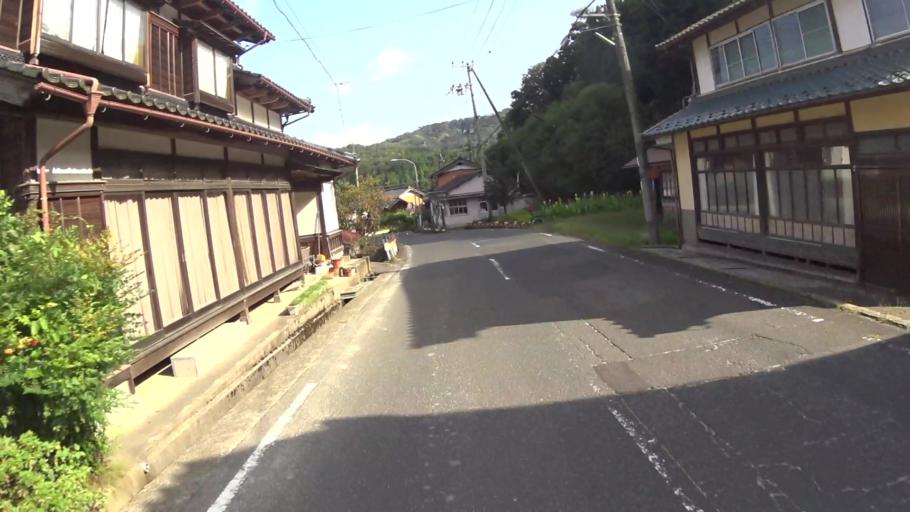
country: JP
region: Kyoto
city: Miyazu
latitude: 35.5717
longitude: 135.1150
